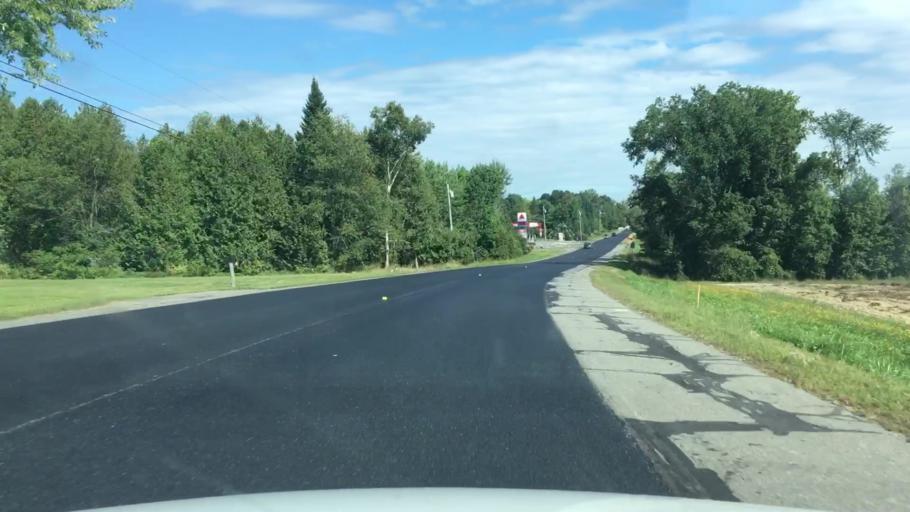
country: US
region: Maine
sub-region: Penobscot County
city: Corinna
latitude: 44.9108
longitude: -69.2651
